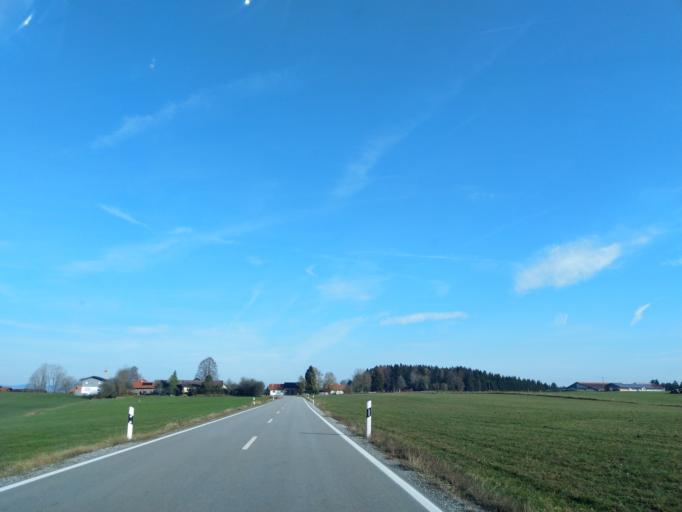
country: DE
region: Bavaria
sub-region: Lower Bavaria
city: Lalling
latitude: 48.8878
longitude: 13.1302
